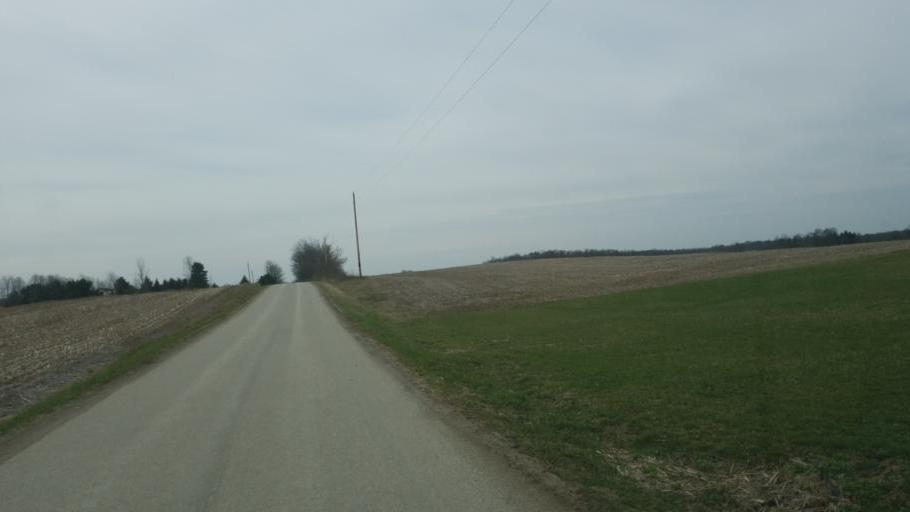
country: US
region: Ohio
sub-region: Knox County
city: Centerburg
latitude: 40.3219
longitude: -82.6483
